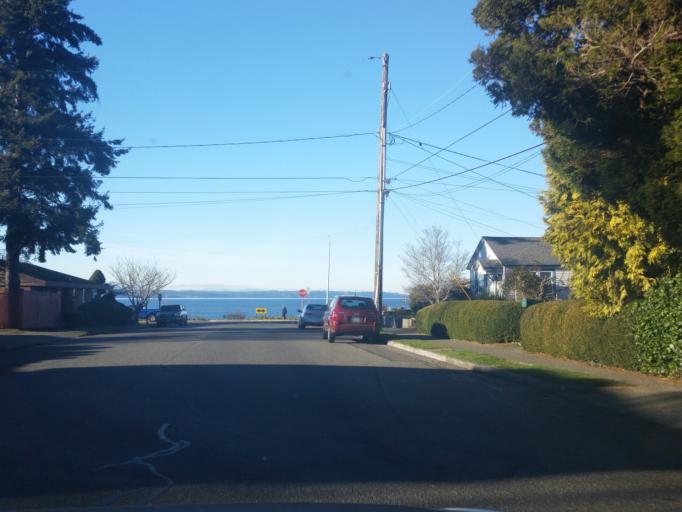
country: US
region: Washington
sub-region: Snohomish County
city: Edmonds
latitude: 47.8139
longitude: -122.3792
